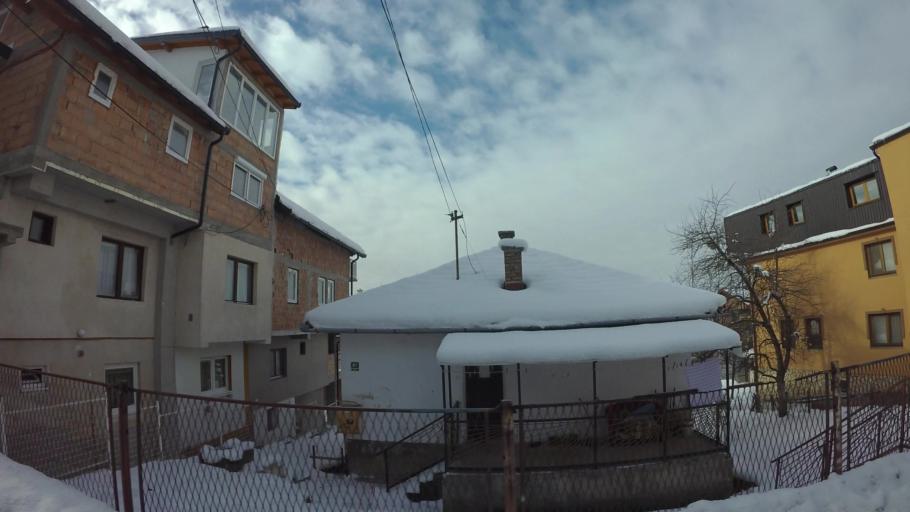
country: BA
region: Federation of Bosnia and Herzegovina
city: Kobilja Glava
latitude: 43.8780
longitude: 18.4174
